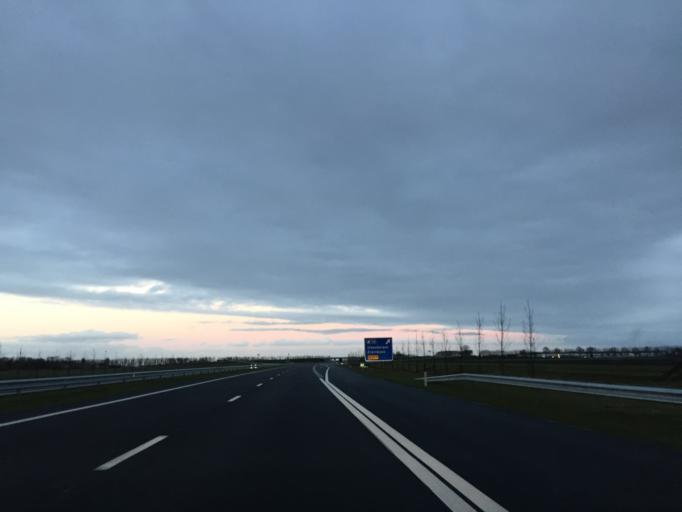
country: NL
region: North Brabant
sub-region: Gemeente Steenbergen
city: Steenbergen
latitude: 51.5835
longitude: 4.2891
